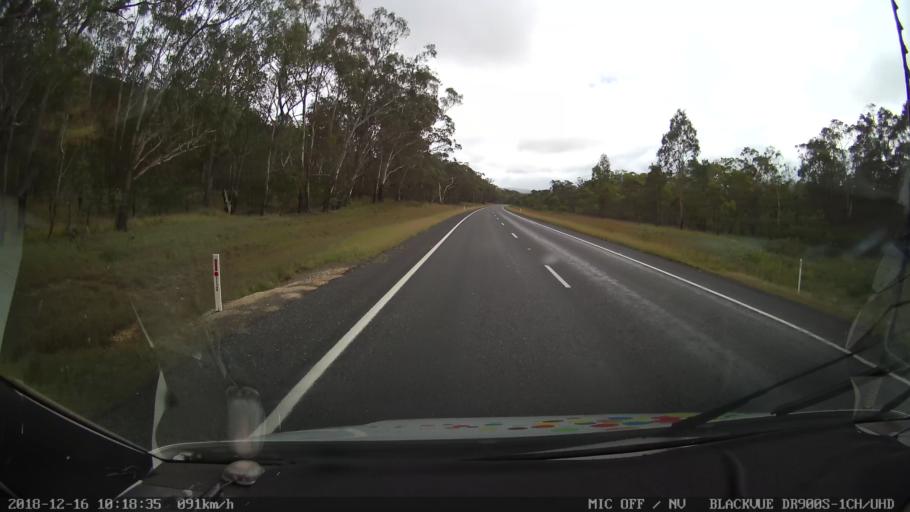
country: AU
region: New South Wales
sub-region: Tenterfield Municipality
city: Carrolls Creek
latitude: -29.2416
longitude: 151.9988
